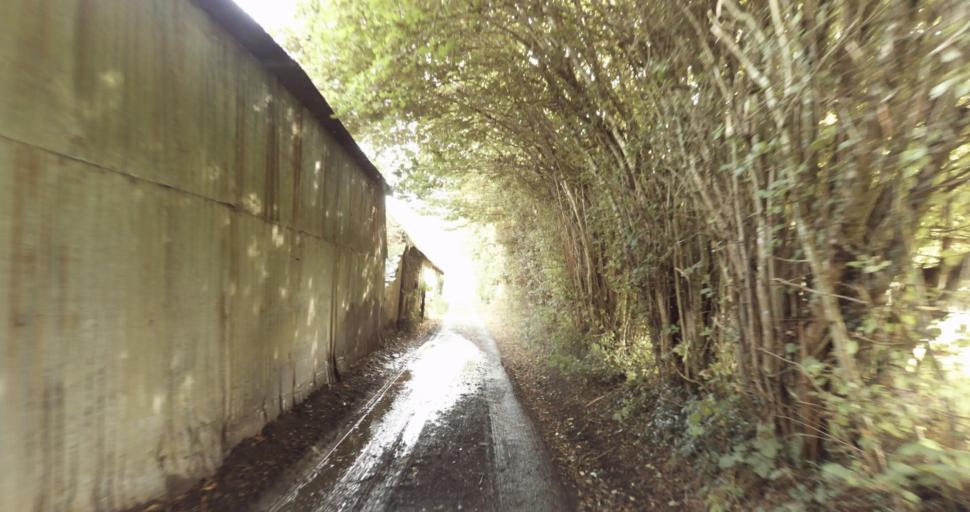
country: FR
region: Lower Normandy
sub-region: Departement de l'Orne
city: Sainte-Gauburge-Sainte-Colombe
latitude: 48.7029
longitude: 0.3714
